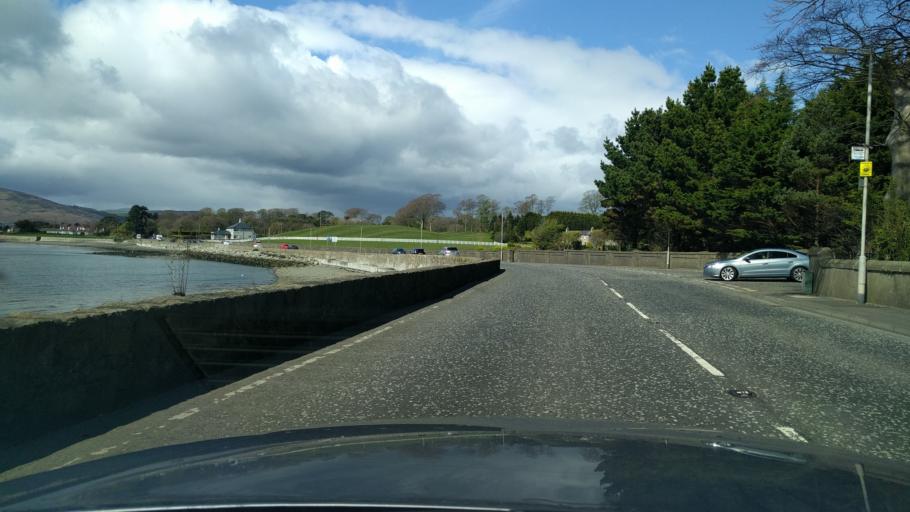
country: GB
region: Northern Ireland
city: Rostrevor
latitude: 54.1001
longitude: -6.2137
